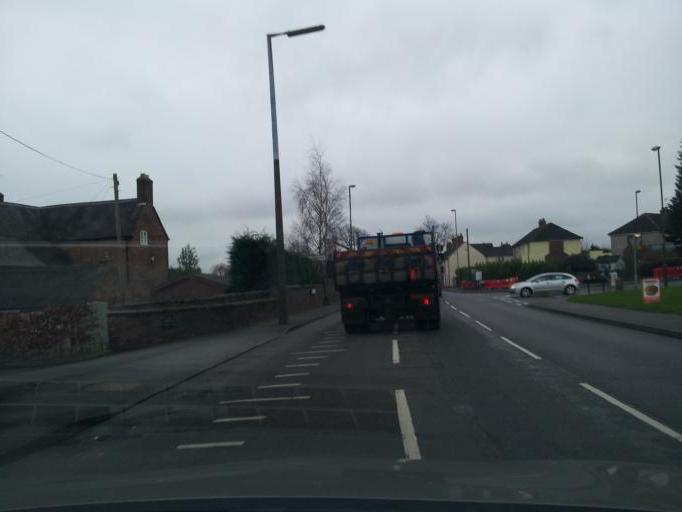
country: GB
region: England
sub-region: Derbyshire
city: Swadlincote
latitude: 52.7872
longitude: -1.5559
